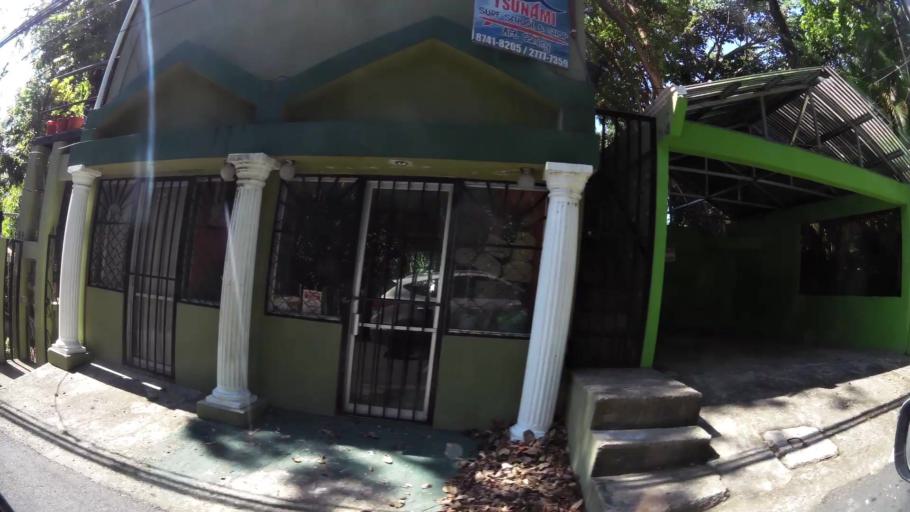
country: CR
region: Puntarenas
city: Quepos
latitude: 9.4042
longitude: -84.1597
